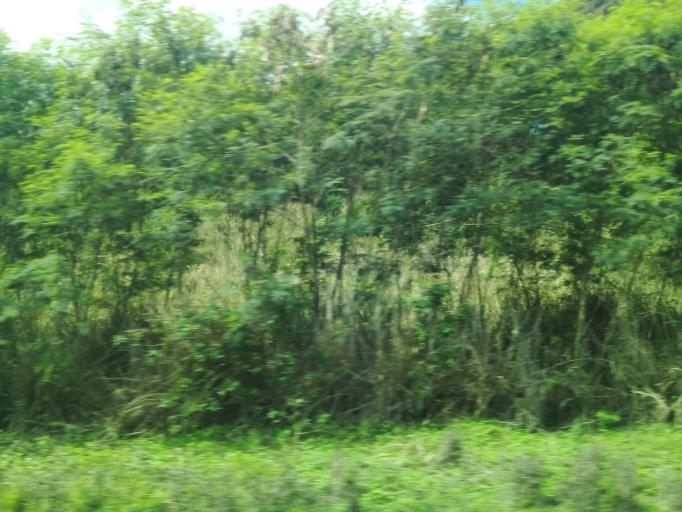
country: BR
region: Minas Gerais
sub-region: Governador Valadares
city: Governador Valadares
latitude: -18.9236
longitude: -42.0249
